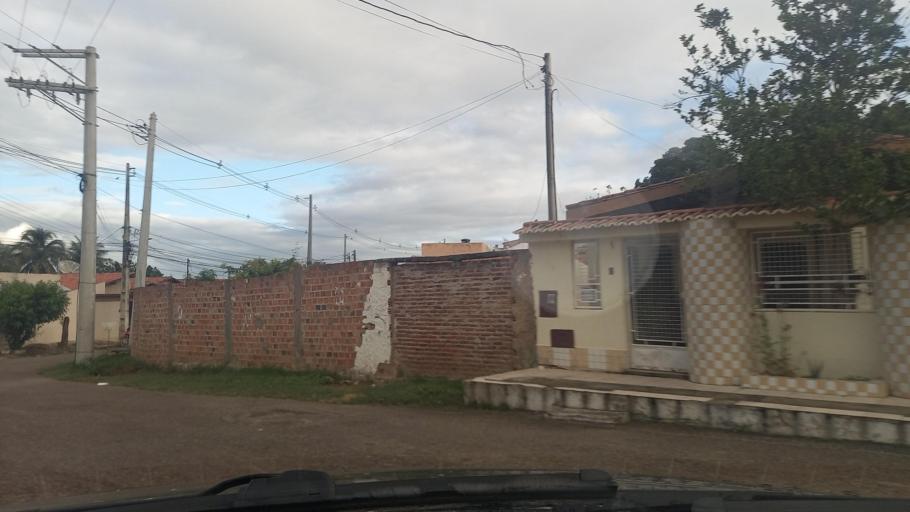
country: BR
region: Bahia
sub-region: Paulo Afonso
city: Paulo Afonso
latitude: -9.3942
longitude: -38.2151
